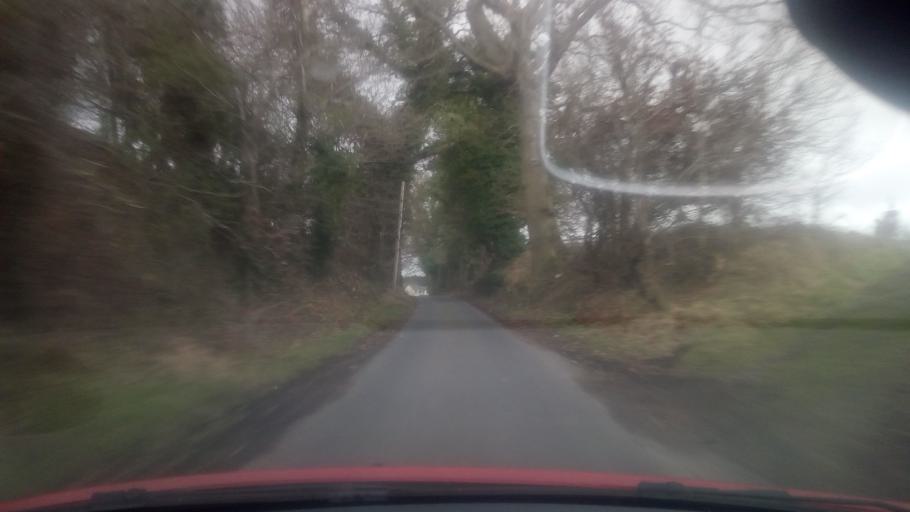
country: GB
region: Scotland
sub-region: The Scottish Borders
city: Jedburgh
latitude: 55.4764
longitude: -2.5430
